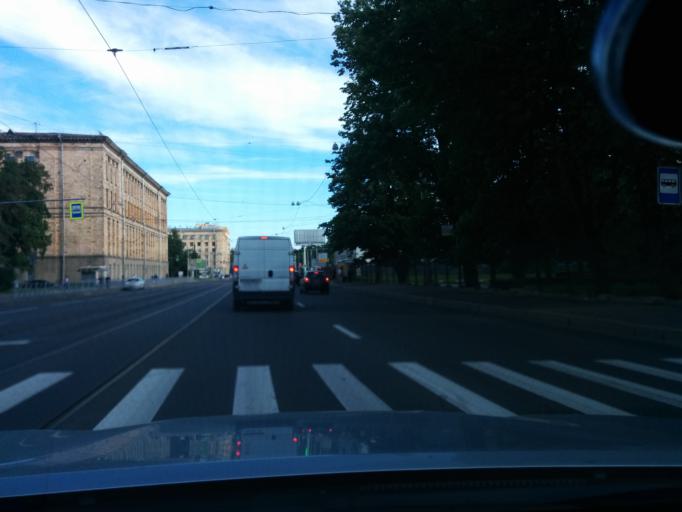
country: RU
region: Leningrad
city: Svetlanovskiy
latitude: 60.0056
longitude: 30.3268
